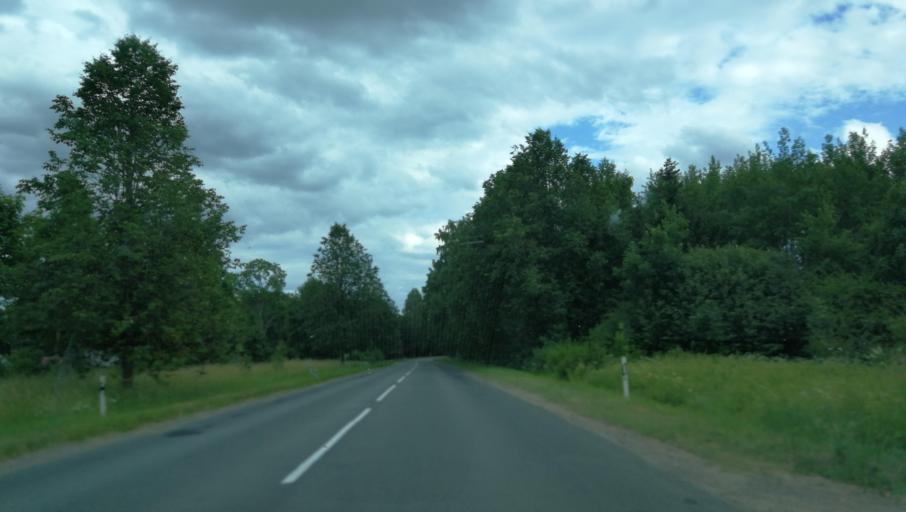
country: LV
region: Rujienas
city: Rujiena
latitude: 57.8758
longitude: 25.3631
